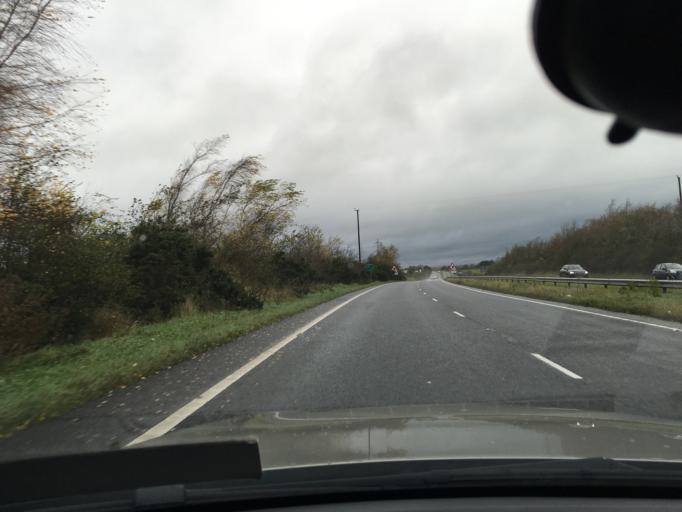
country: GB
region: Northern Ireland
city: Carnmoney
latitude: 54.7128
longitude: -5.9682
